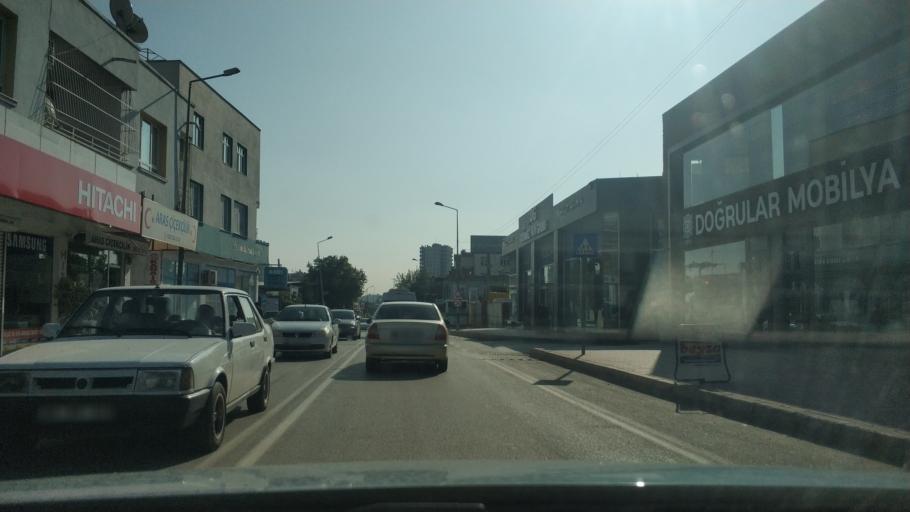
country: TR
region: Adana
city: Seyhan
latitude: 37.0151
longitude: 35.3016
